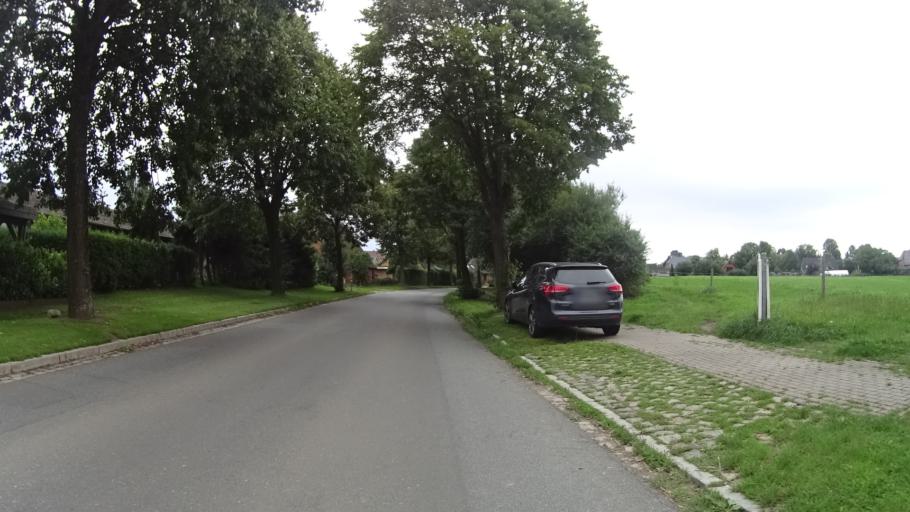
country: DE
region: Schleswig-Holstein
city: Duvensee
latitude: 53.6951
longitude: 10.5679
